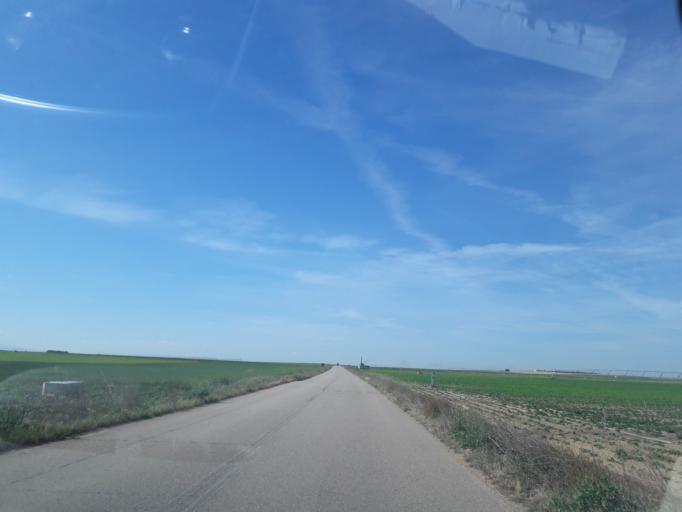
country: ES
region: Castille and Leon
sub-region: Provincia de Salamanca
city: Villoruela
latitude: 41.0317
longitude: -5.3909
